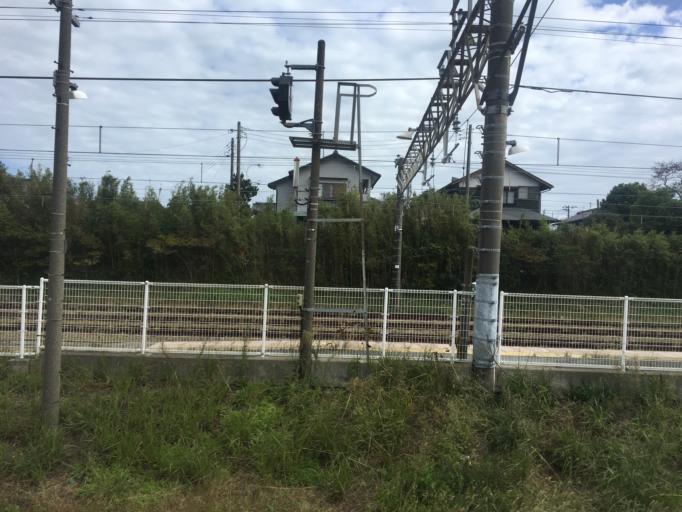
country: JP
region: Chiba
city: Ohara
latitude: 35.2518
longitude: 140.3910
